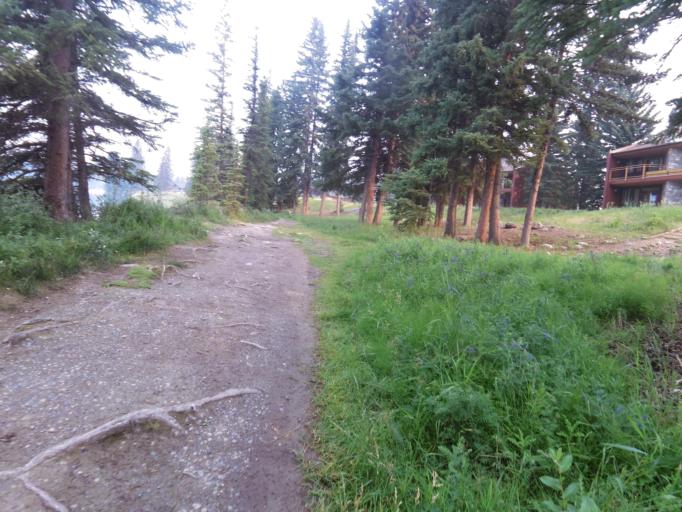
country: CA
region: Alberta
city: Jasper Park Lodge
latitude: 52.8836
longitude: -118.0537
